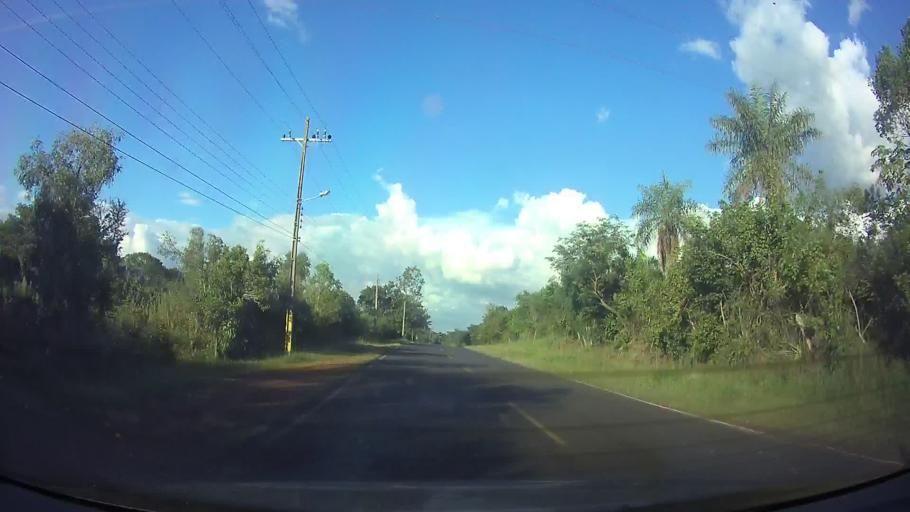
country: PY
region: Cordillera
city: Emboscada
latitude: -25.1810
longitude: -57.2941
